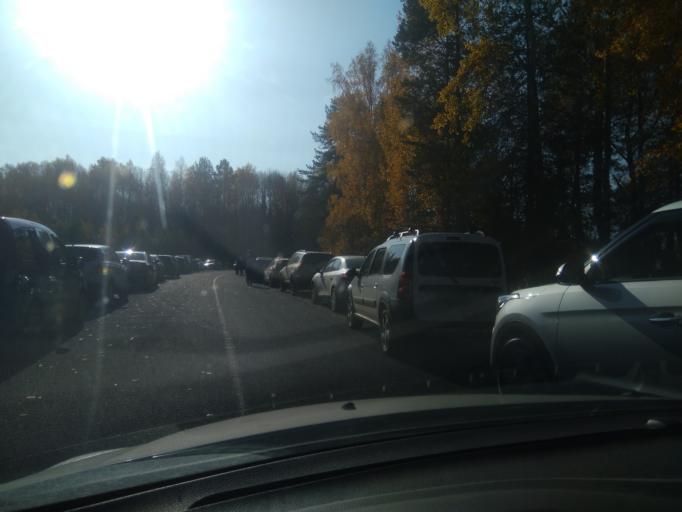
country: RU
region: Sverdlovsk
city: Mikhaylovsk
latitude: 56.5290
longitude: 59.2267
